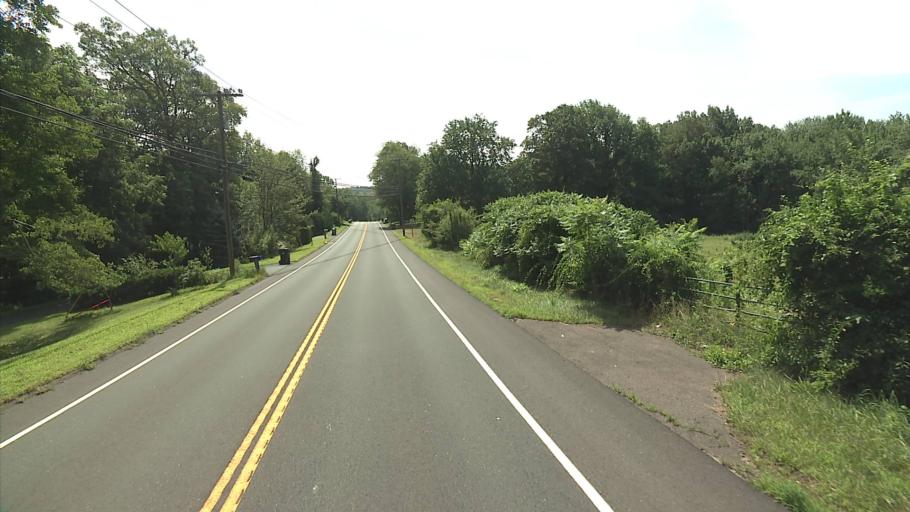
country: US
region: Connecticut
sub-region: Tolland County
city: Rockville
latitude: 41.8378
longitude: -72.4078
